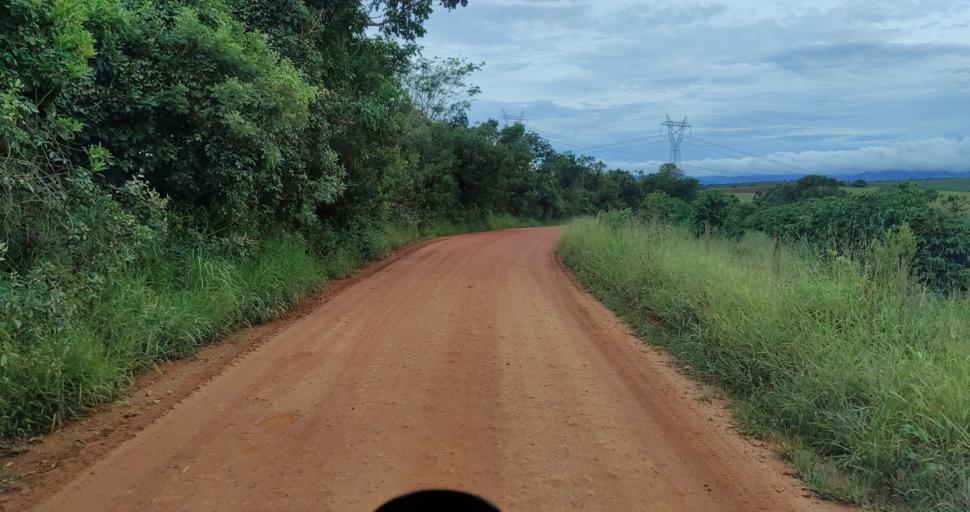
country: BR
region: Minas Gerais
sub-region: Piui
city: Piui
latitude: -20.2861
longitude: -46.3666
